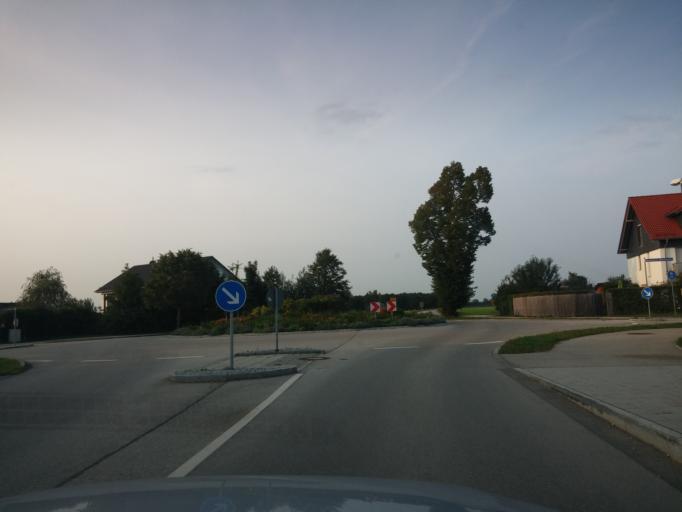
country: DE
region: Bavaria
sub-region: Upper Bavaria
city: Grasbrunn
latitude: 48.0608
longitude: 11.7721
